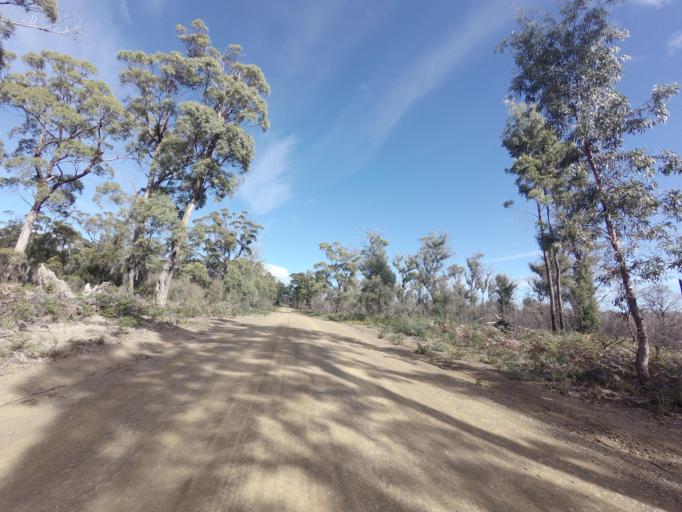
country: AU
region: Tasmania
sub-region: Clarence
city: Sandford
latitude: -42.9782
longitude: 147.7166
